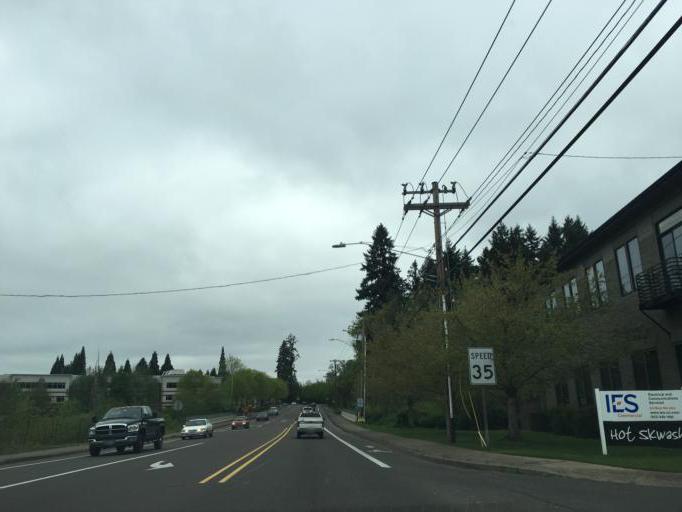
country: US
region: Oregon
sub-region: Washington County
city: Durham
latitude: 45.4029
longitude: -122.7538
